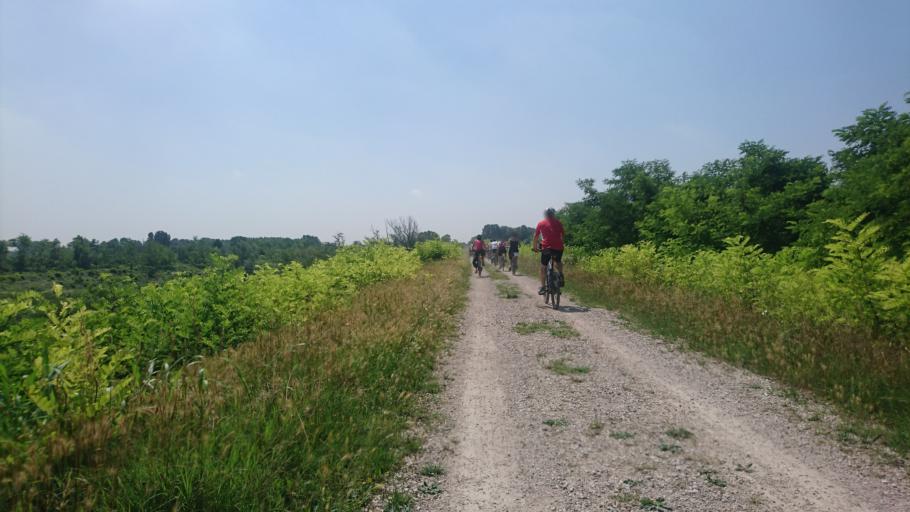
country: IT
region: Veneto
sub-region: Provincia di Padova
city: Oltre Brenta
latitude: 45.4001
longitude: 12.0036
